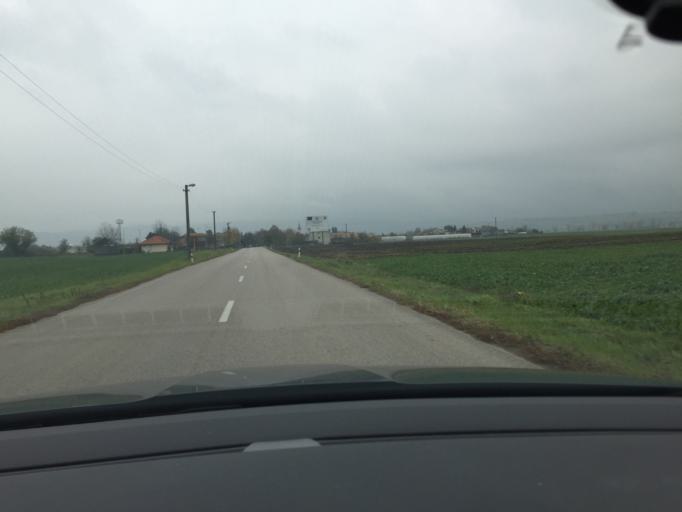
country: HU
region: Komarom-Esztergom
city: Esztergom
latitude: 47.8964
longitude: 18.7542
